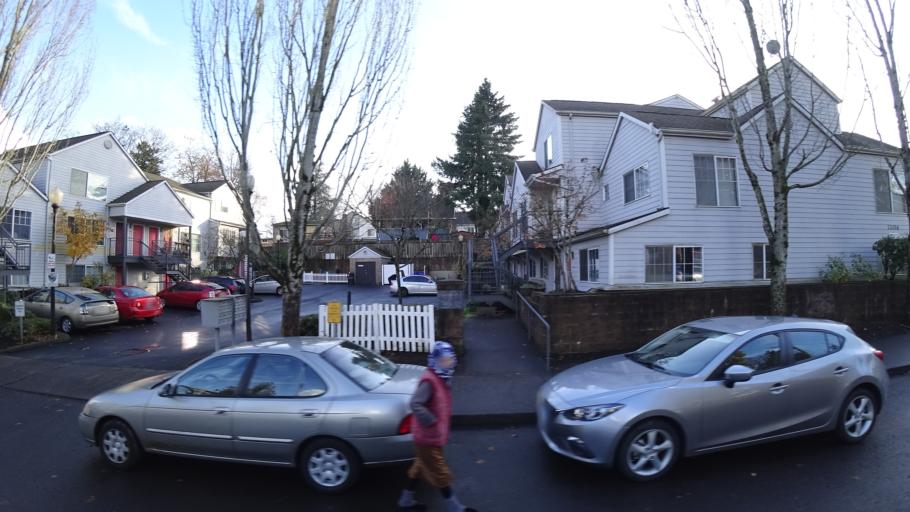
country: US
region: Oregon
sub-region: Multnomah County
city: Lents
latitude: 45.5218
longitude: -122.5390
